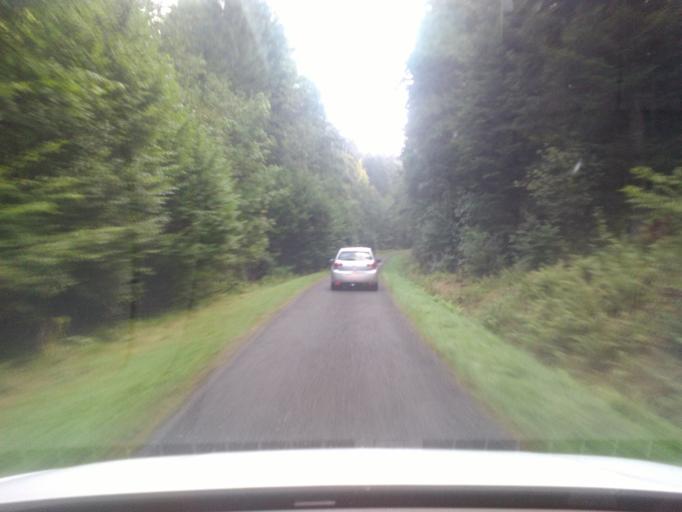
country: FR
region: Lorraine
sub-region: Departement des Vosges
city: Moyenmoutier
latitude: 48.4074
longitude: 6.9149
